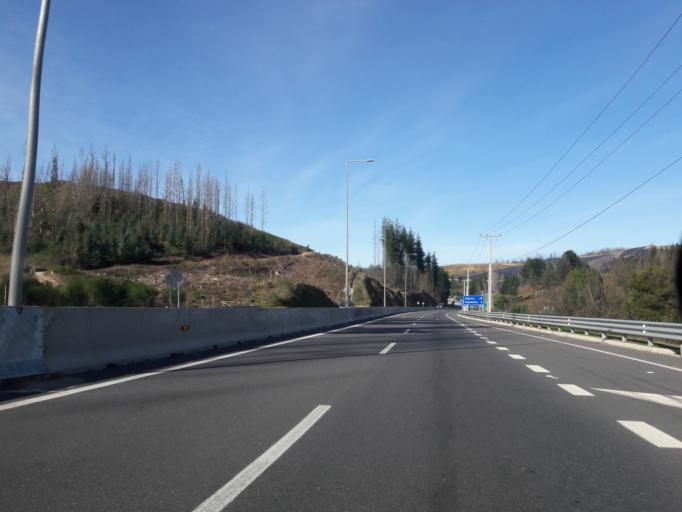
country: CL
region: Biobio
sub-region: Provincia de Concepcion
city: Penco
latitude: -36.8589
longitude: -72.8603
